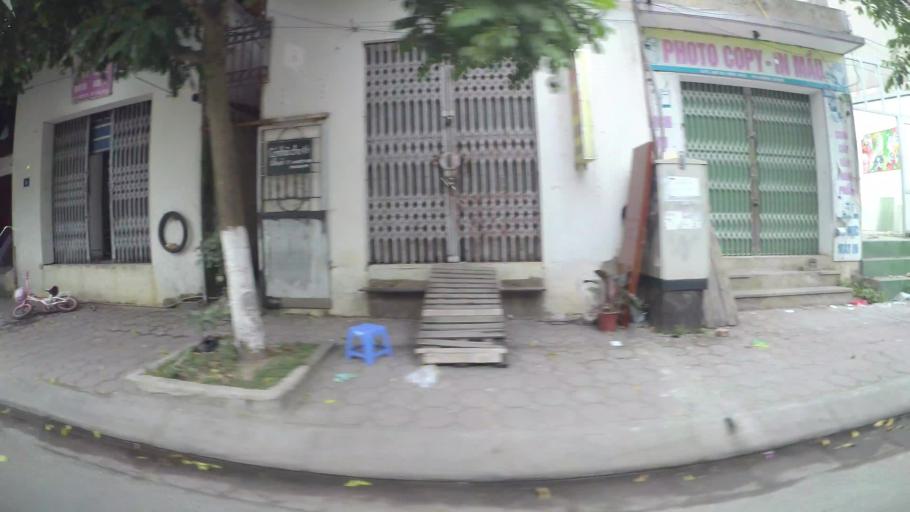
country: VN
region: Ha Noi
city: Trau Quy
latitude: 21.0461
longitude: 105.9249
